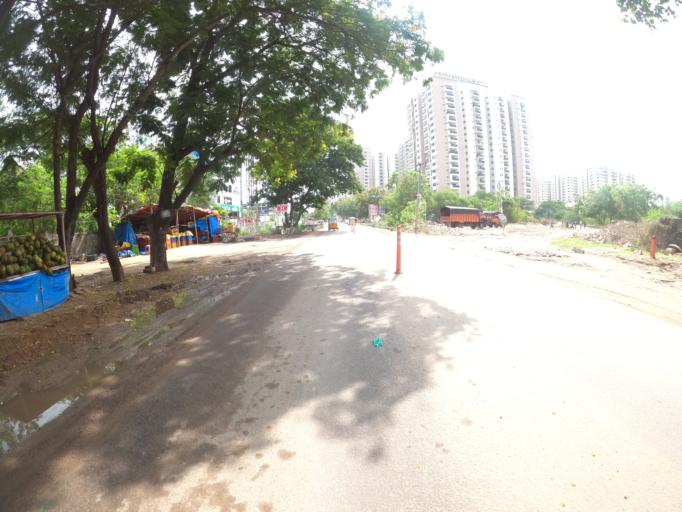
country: IN
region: Telangana
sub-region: Medak
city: Serilingampalle
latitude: 17.3880
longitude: 78.3432
